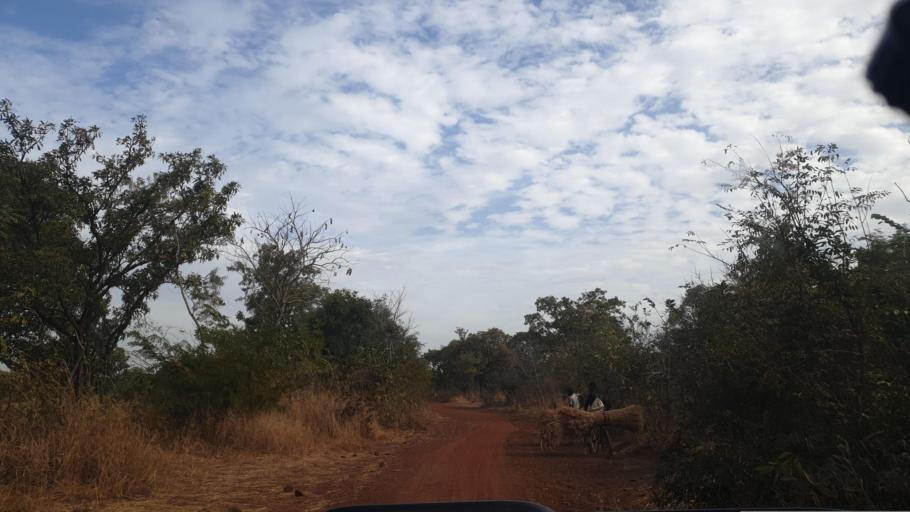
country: ML
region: Sikasso
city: Yanfolila
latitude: 11.4029
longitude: -8.0146
